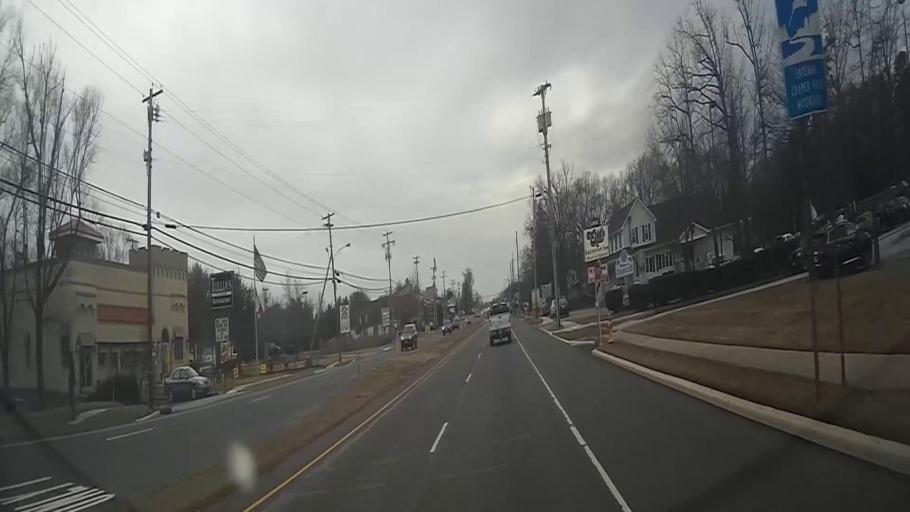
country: US
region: New Jersey
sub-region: Camden County
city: Berlin
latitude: 39.8196
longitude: -74.9292
